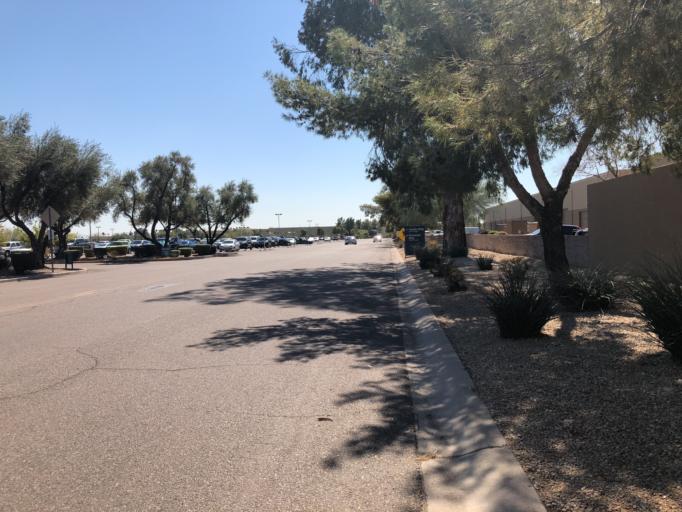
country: US
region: Arizona
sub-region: Maricopa County
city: Scottsdale
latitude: 33.4648
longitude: -111.9063
